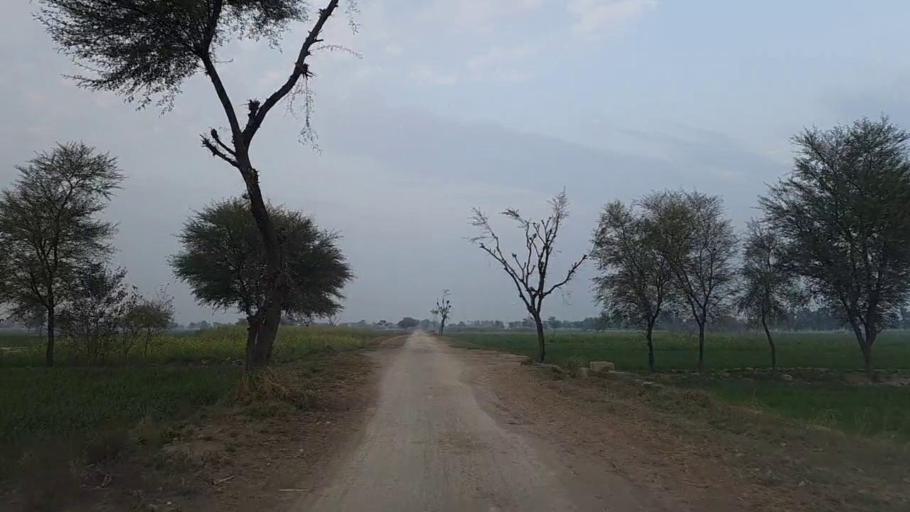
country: PK
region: Sindh
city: Jam Sahib
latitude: 26.2926
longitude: 68.5934
